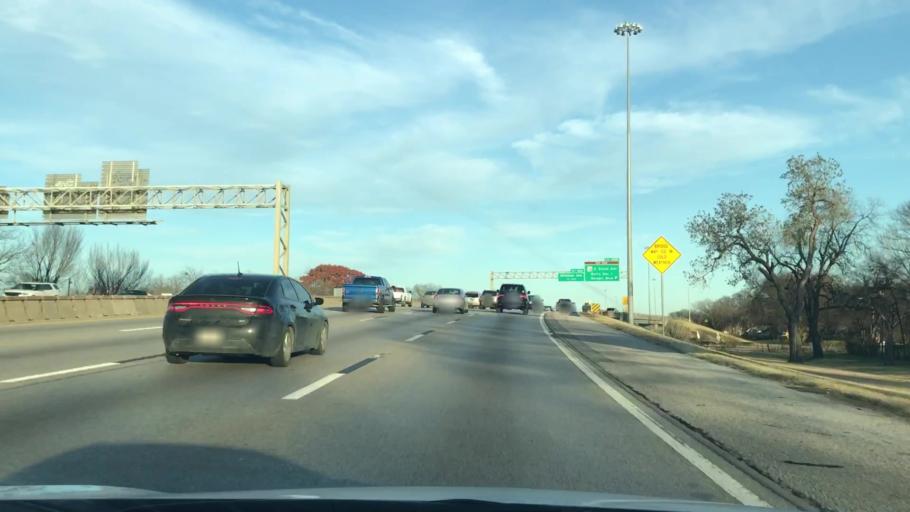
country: US
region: Texas
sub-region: Dallas County
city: Dallas
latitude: 32.7905
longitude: -96.7599
